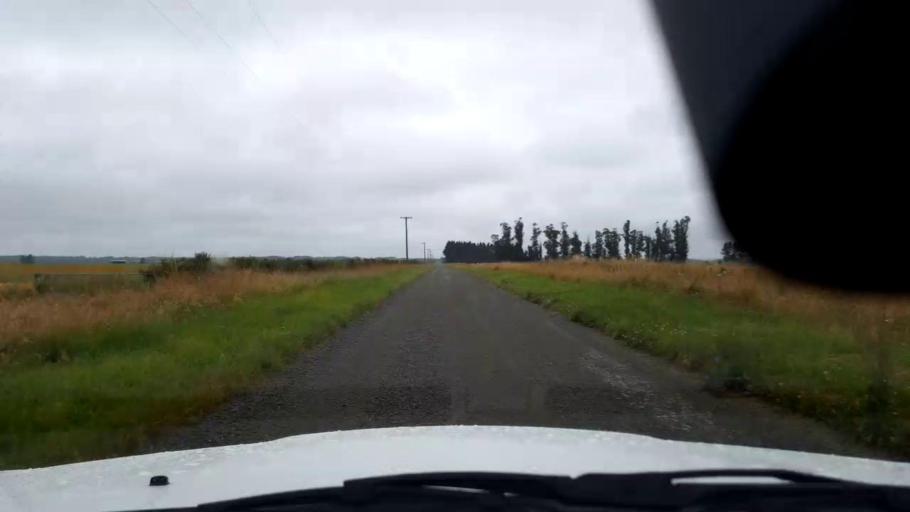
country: NZ
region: Canterbury
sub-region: Timaru District
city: Pleasant Point
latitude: -44.2344
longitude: 171.2023
